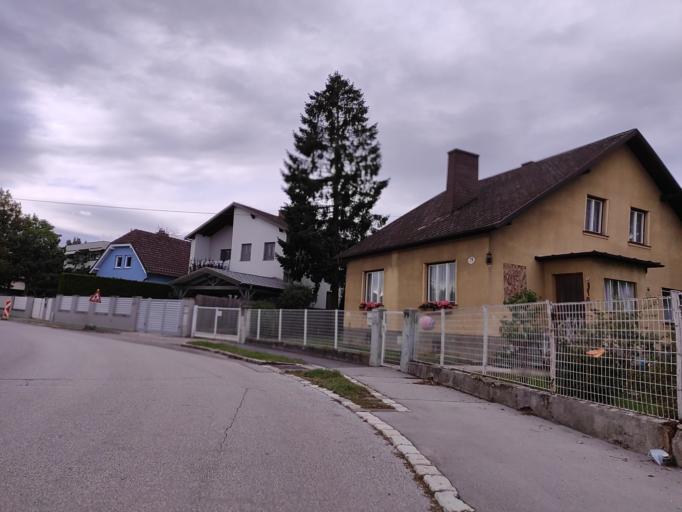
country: AT
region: Lower Austria
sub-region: Politischer Bezirk Baden
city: Pfaffstatten
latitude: 48.0069
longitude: 16.2503
